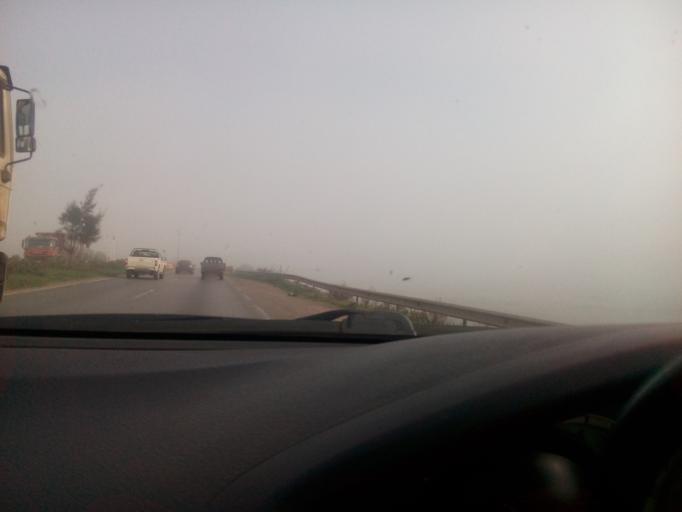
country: DZ
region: Oran
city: Es Senia
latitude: 35.6149
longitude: -0.7214
